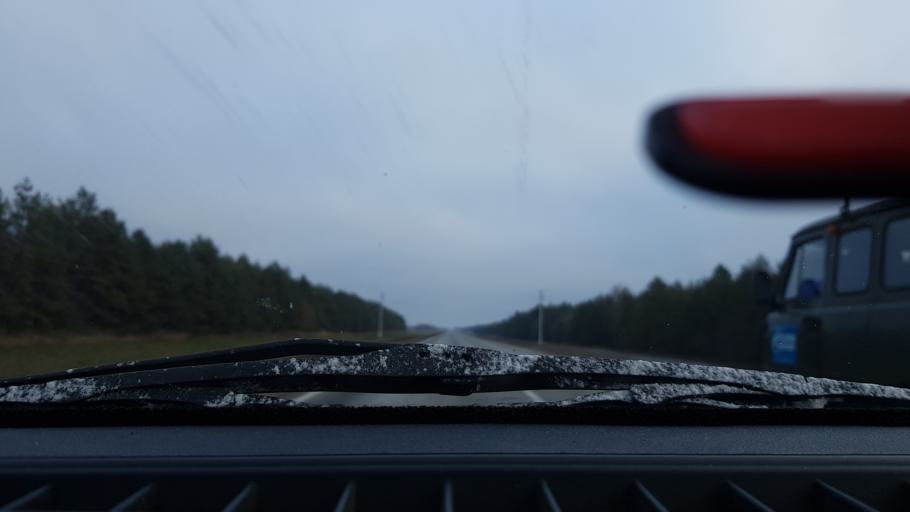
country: RU
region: Tatarstan
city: Kuybyshevskiy Zaton
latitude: 54.9496
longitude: 49.4593
